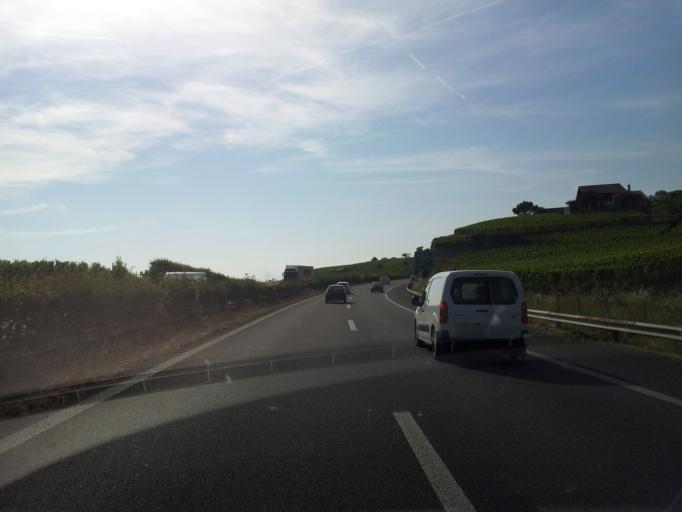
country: CH
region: Vaud
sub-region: Riviera-Pays-d'Enhaut District
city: Blonay
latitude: 46.4577
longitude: 6.8833
